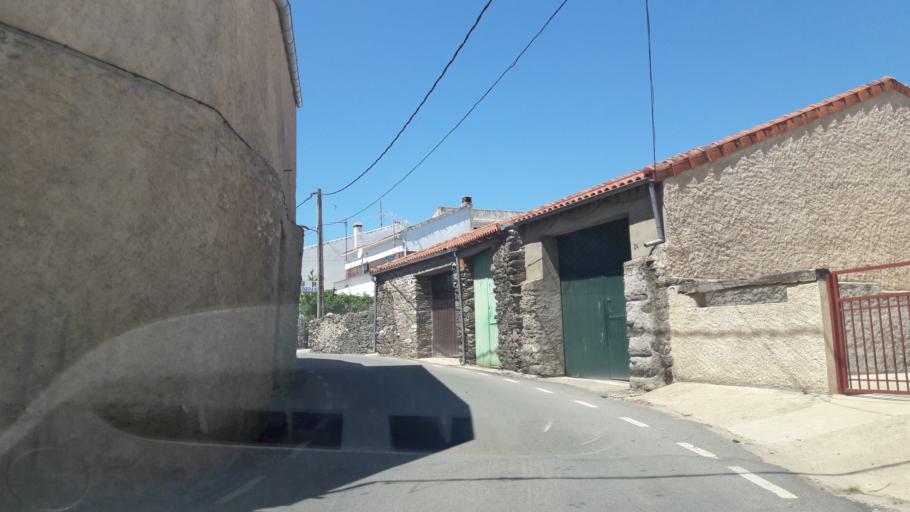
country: ES
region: Castille and Leon
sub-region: Provincia de Salamanca
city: Endrinal
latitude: 40.5919
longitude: -5.8042
